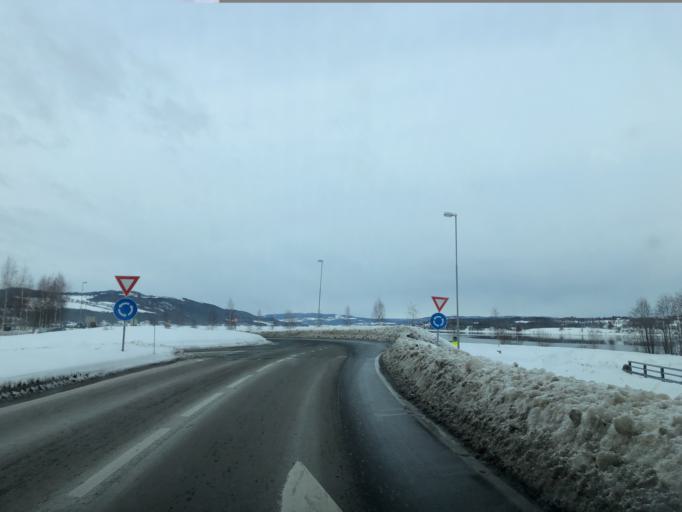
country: NO
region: Oppland
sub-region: Gjovik
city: Gjovik
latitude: 60.7979
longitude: 10.6963
